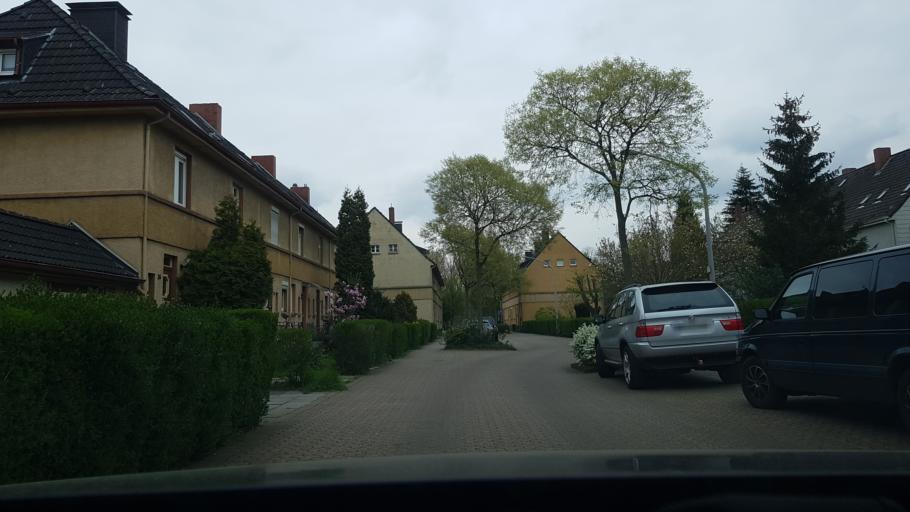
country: DE
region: North Rhine-Westphalia
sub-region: Regierungsbezirk Dusseldorf
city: Hochfeld
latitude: 51.3938
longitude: 6.7993
